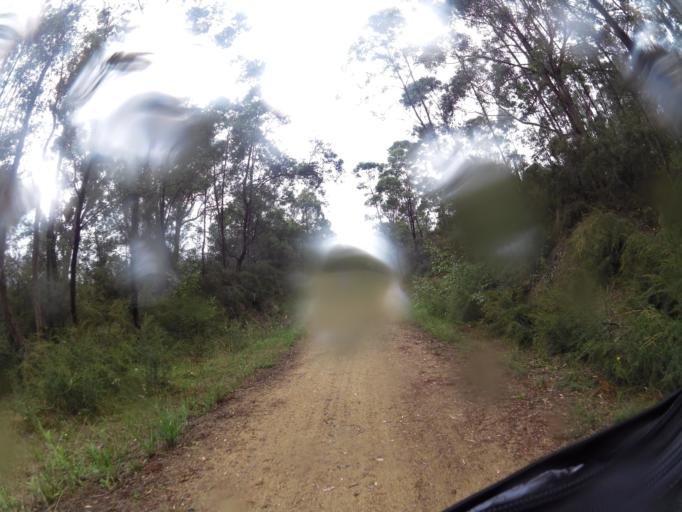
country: AU
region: Victoria
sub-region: East Gippsland
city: Bairnsdale
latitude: -37.7458
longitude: 147.8103
